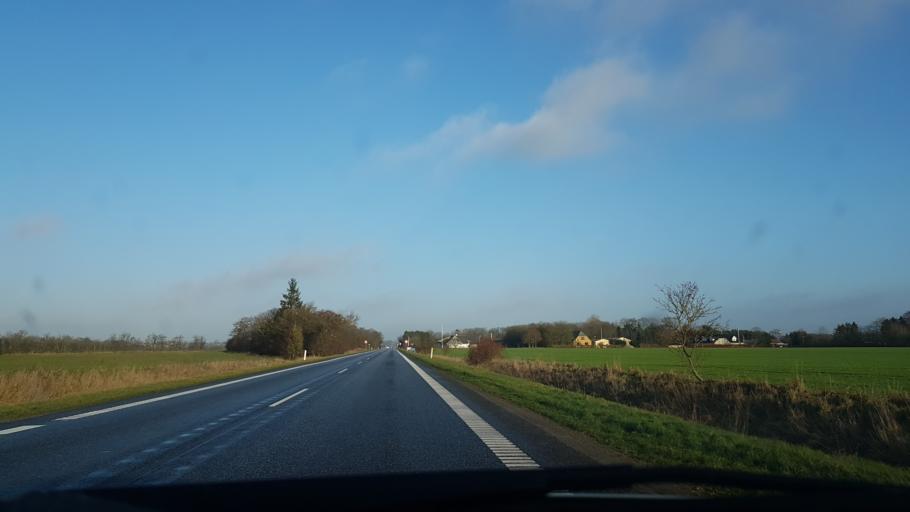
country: DK
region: South Denmark
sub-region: Tonder Kommune
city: Toftlund
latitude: 55.2296
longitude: 9.1177
